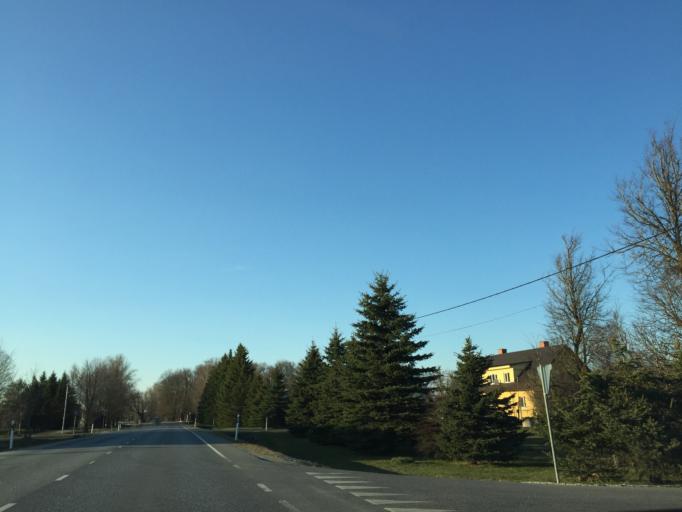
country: EE
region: Ida-Virumaa
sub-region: Johvi vald
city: Johvi
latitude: 59.2689
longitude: 27.5134
